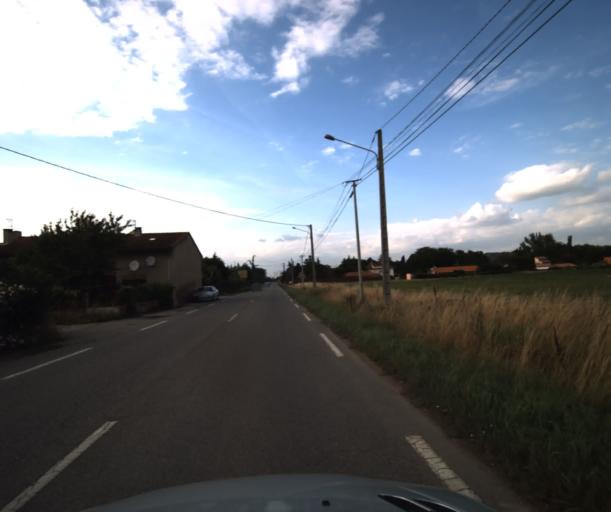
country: FR
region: Midi-Pyrenees
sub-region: Departement de la Haute-Garonne
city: Labarthe-sur-Leze
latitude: 43.4661
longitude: 1.3977
